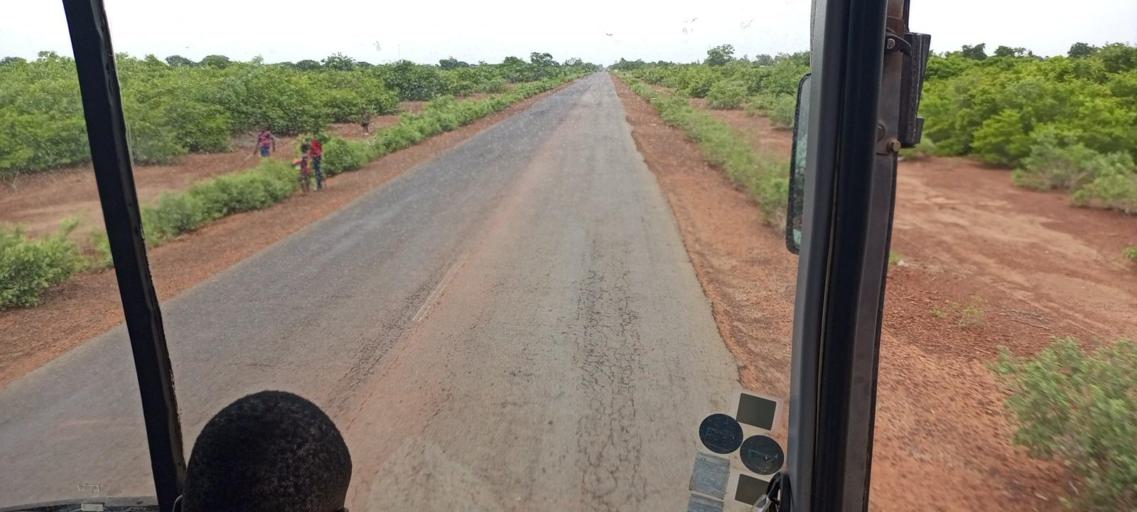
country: ML
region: Sikasso
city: Koutiala
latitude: 12.5505
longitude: -5.5841
